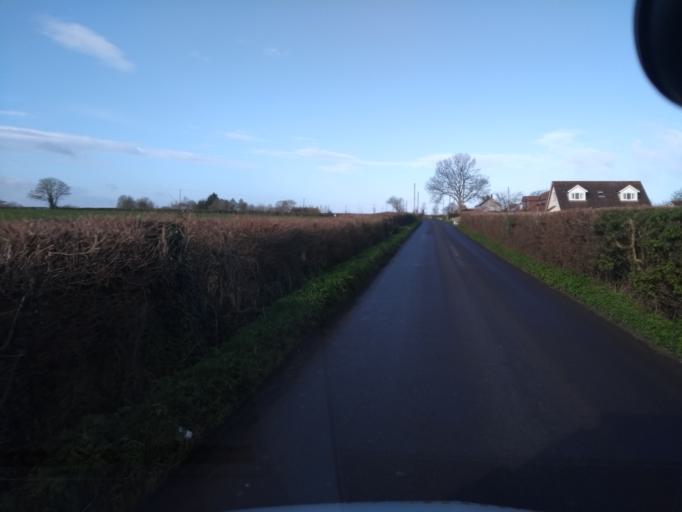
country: GB
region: England
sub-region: Somerset
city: Woolavington
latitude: 51.1575
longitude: -2.9069
